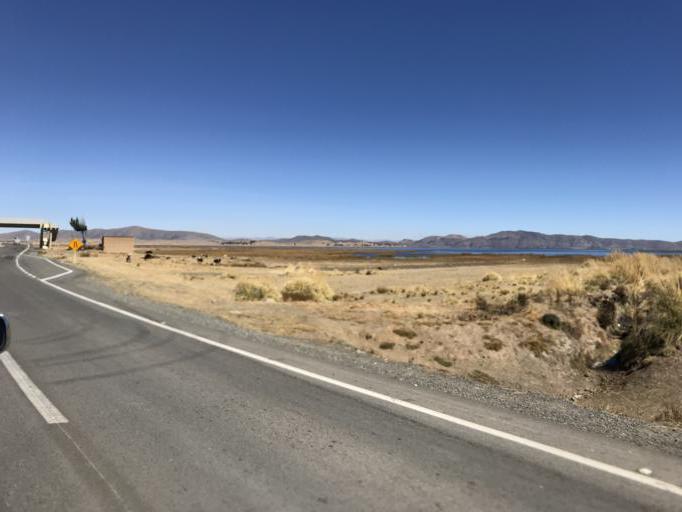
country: BO
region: La Paz
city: Huarina
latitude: -16.2363
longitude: -68.5770
